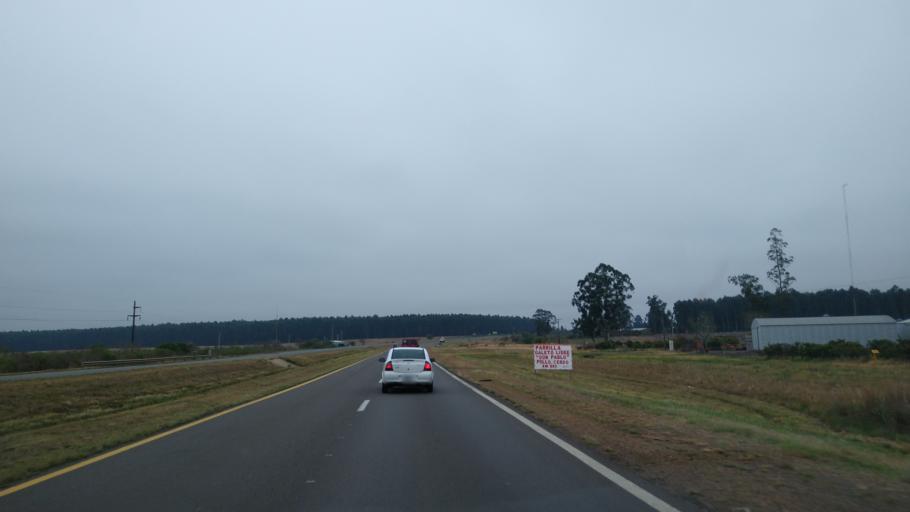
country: AR
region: Entre Rios
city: Chajari
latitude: -30.8361
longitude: -58.0492
